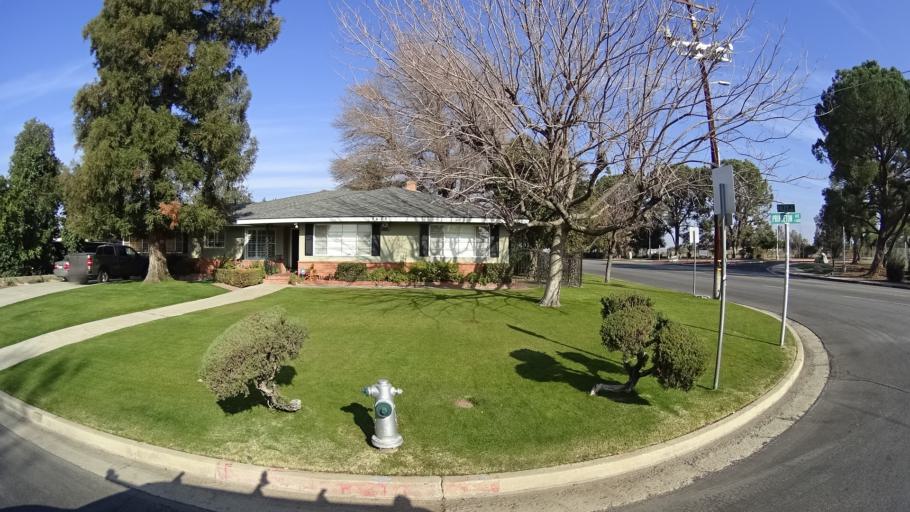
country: US
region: California
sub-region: Kern County
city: Oildale
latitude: 35.4085
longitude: -118.9766
